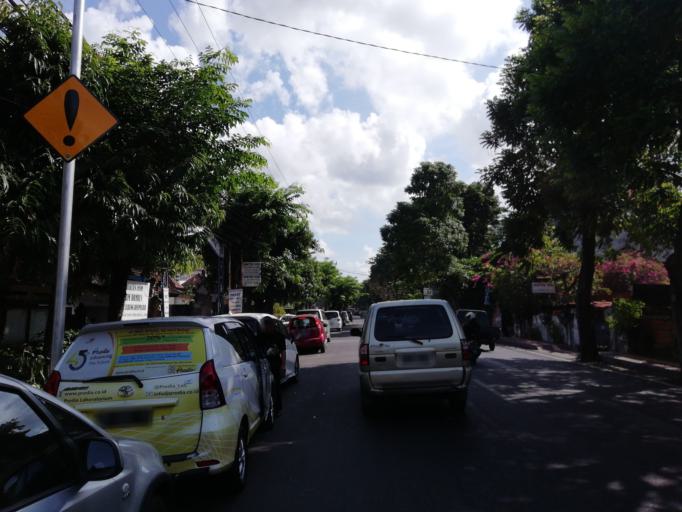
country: ID
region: Bali
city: Denpasar
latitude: -8.6723
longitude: 115.2155
